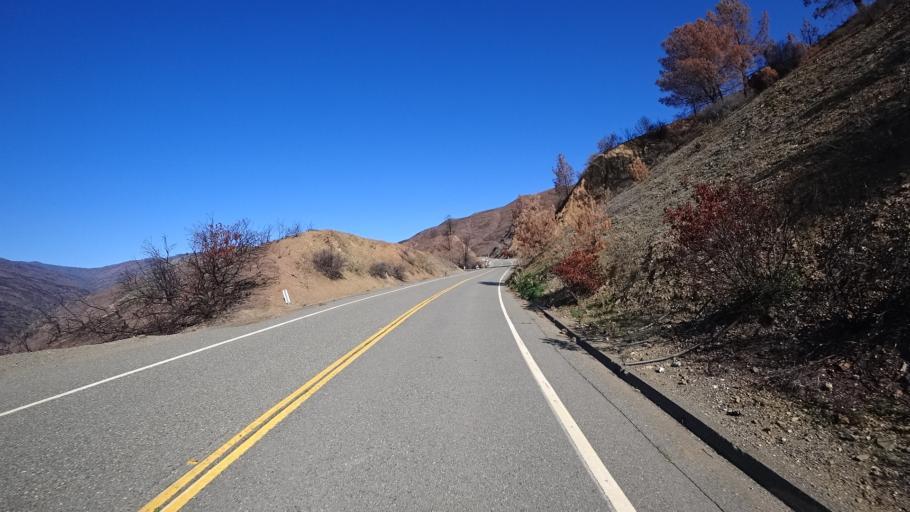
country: US
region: California
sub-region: Glenn County
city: Orland
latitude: 39.6448
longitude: -122.6086
